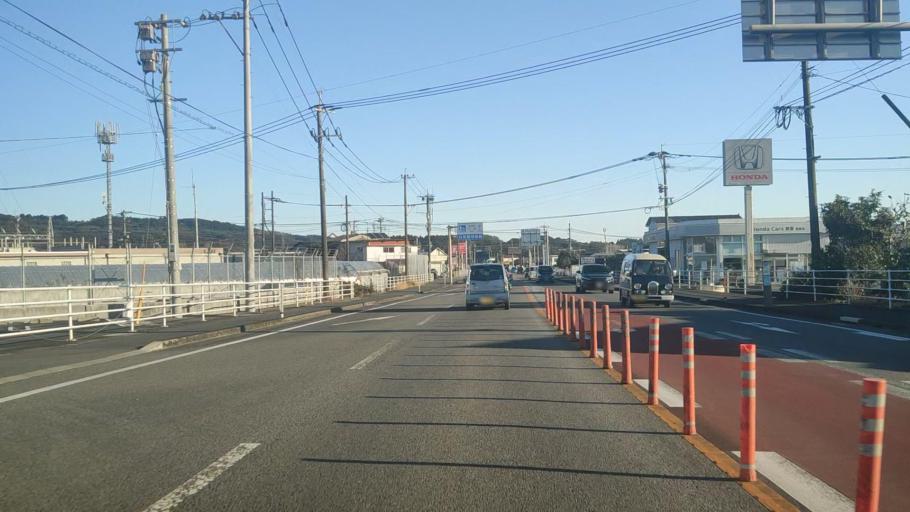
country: JP
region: Miyazaki
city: Takanabe
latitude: 32.2552
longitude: 131.5543
